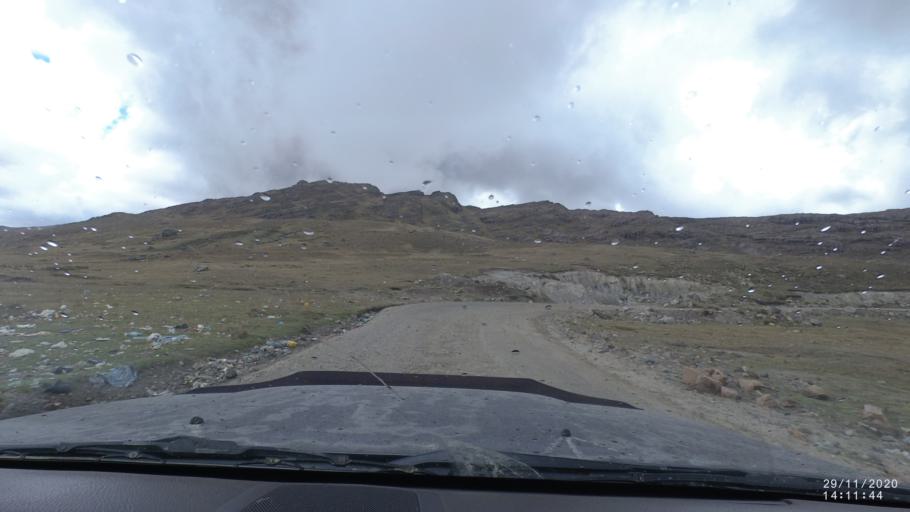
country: BO
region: Cochabamba
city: Sipe Sipe
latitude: -17.2352
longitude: -66.3911
